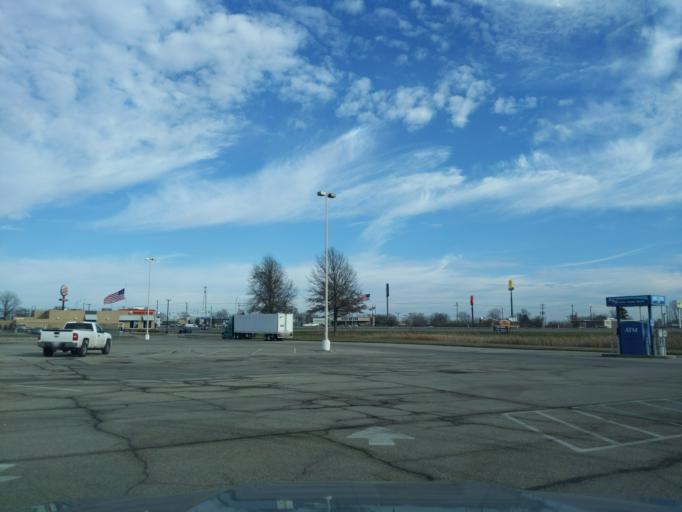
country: US
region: Indiana
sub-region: Decatur County
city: Greensburg
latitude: 39.3558
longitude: -85.4829
